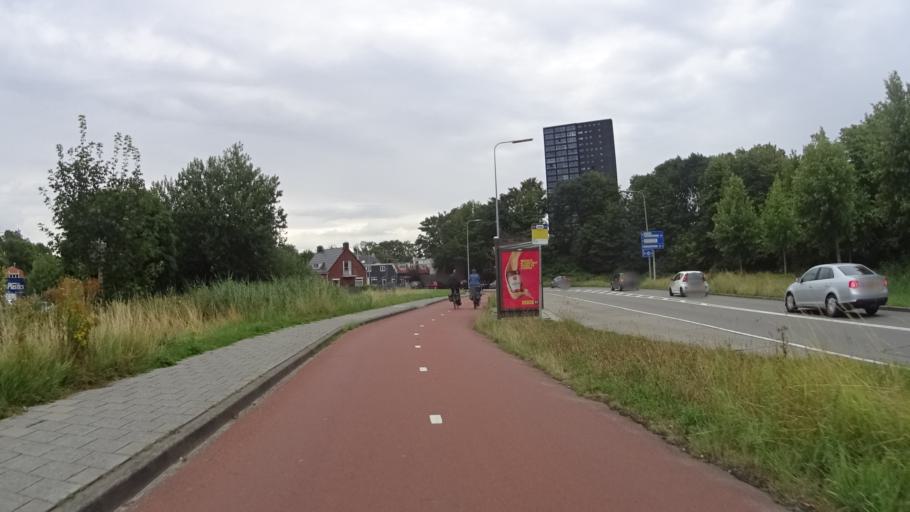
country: NL
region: Groningen
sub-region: Gemeente Groningen
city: Oosterpark
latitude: 53.2262
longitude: 6.5954
